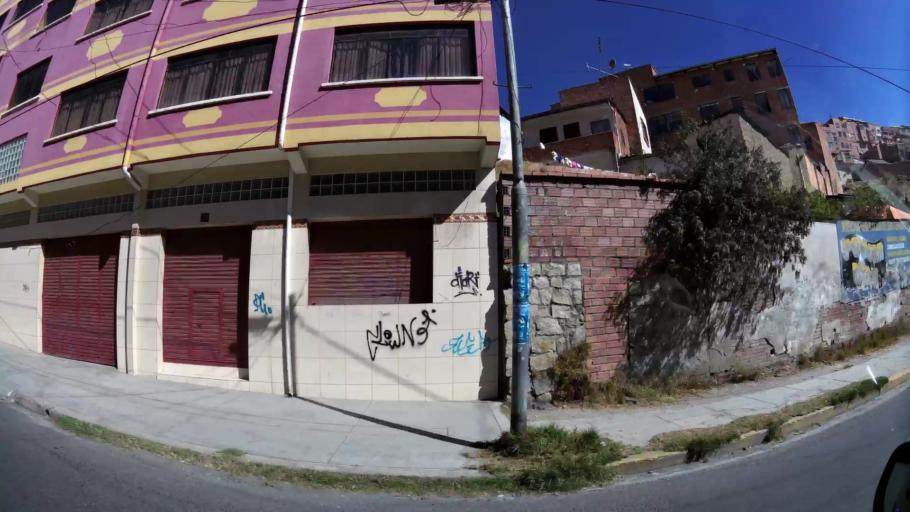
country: BO
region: La Paz
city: La Paz
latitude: -16.4880
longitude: -68.1485
